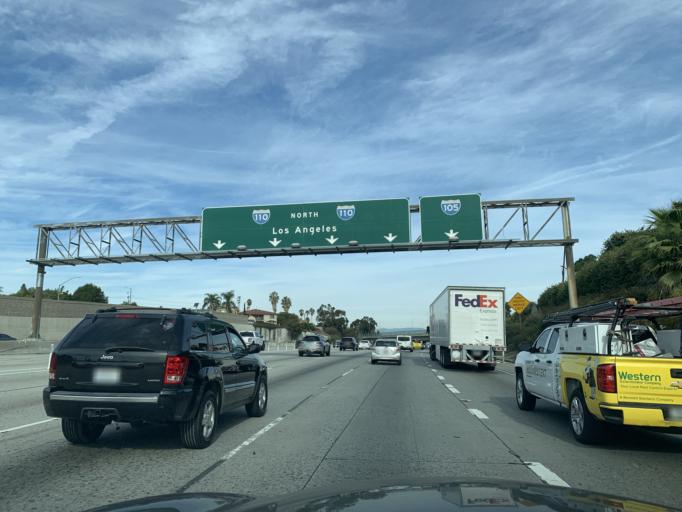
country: US
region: California
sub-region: Los Angeles County
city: West Athens
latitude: 33.9177
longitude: -118.2849
